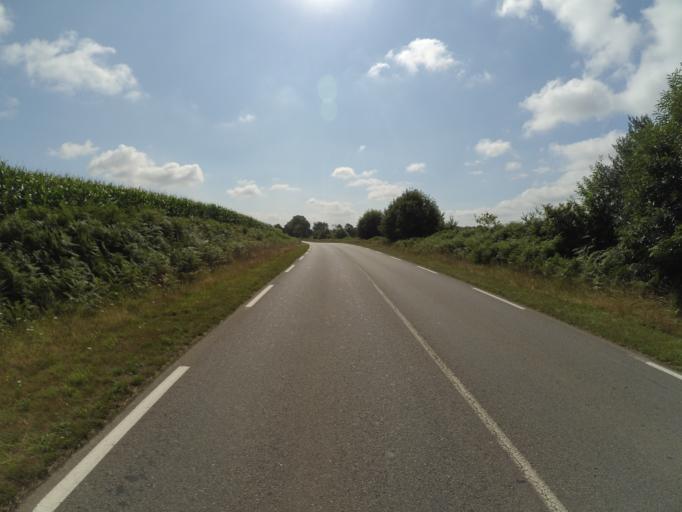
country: FR
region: Brittany
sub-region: Departement du Finistere
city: Bannalec
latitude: 47.9412
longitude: -3.7566
